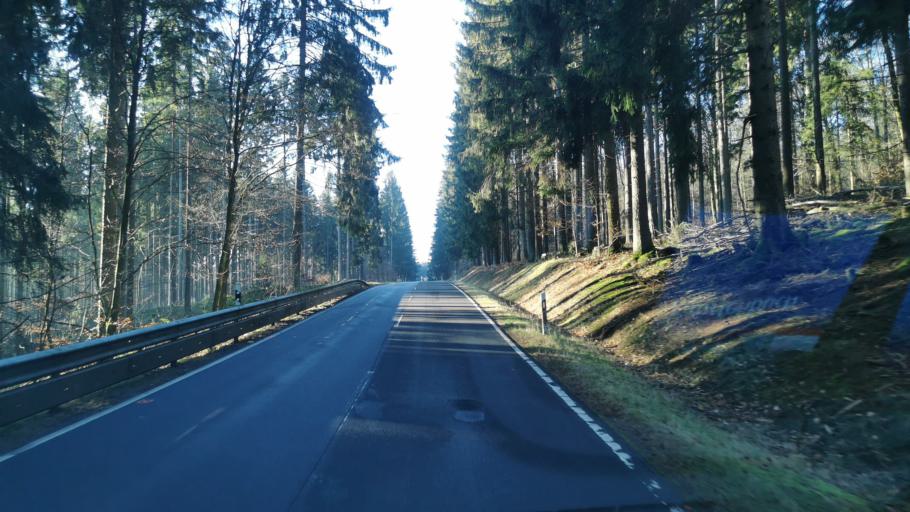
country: DE
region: Rheinland-Pfalz
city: Weidenbach
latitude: 50.1194
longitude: 6.7043
